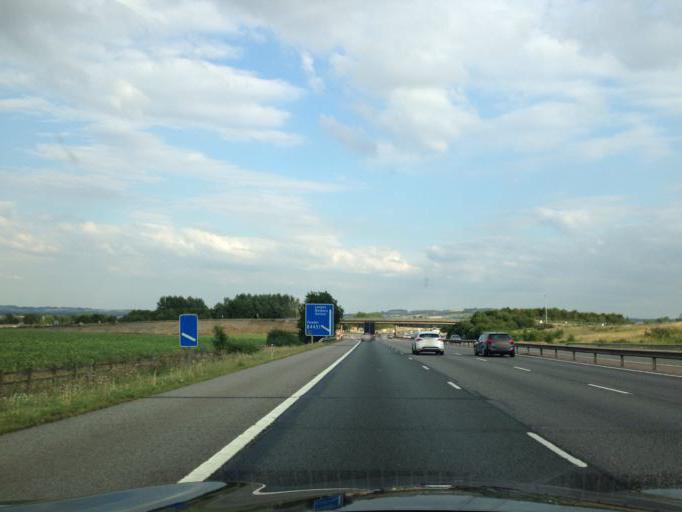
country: GB
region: England
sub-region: Warwickshire
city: Harbury
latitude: 52.1948
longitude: -1.4628
